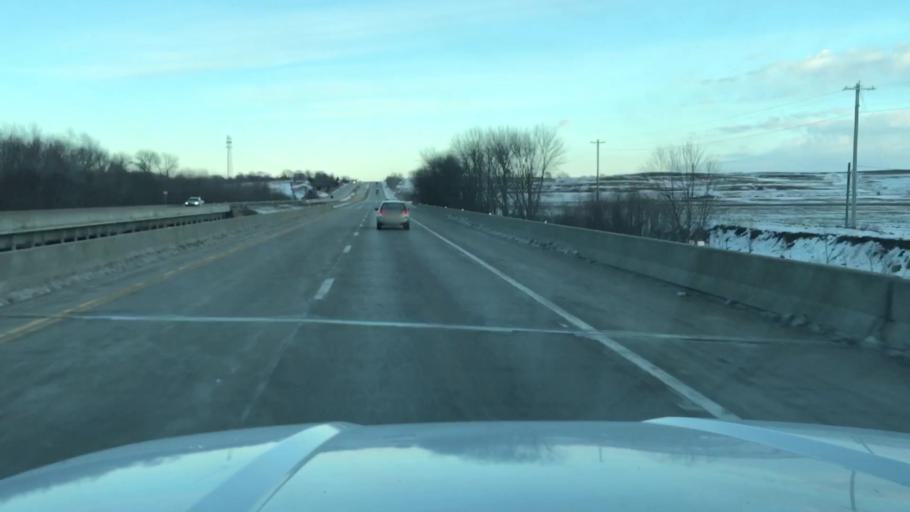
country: US
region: Missouri
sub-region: Clinton County
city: Gower
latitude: 39.7473
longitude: -94.6621
